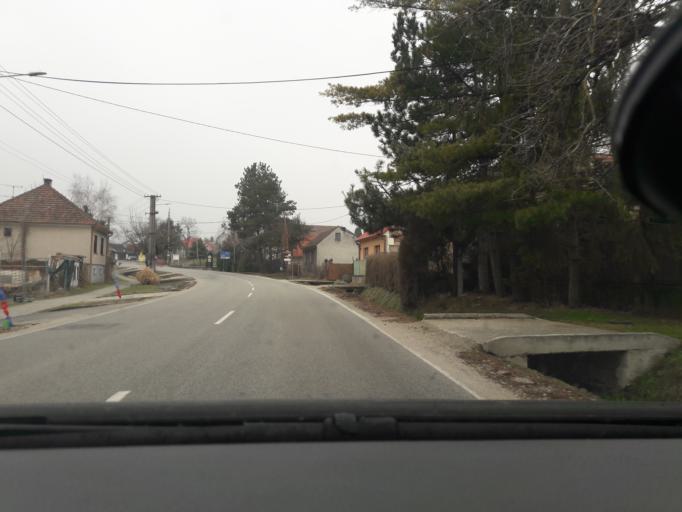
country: SK
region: Trnavsky
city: Smolenice
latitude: 48.4940
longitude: 17.4186
